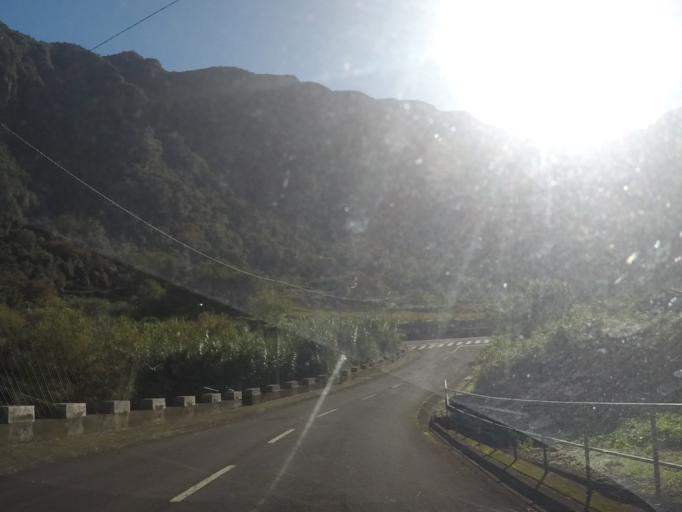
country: PT
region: Madeira
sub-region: Santana
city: Santana
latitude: 32.8024
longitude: -16.9601
